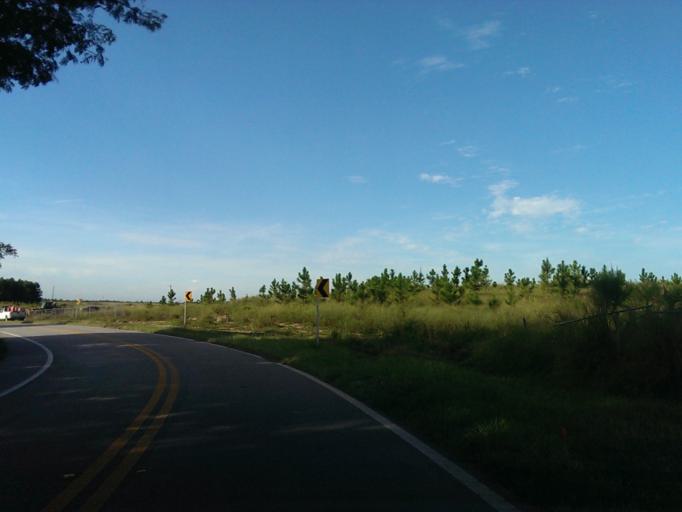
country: US
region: Florida
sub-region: Polk County
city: Citrus Ridge
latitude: 28.4271
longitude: -81.6187
